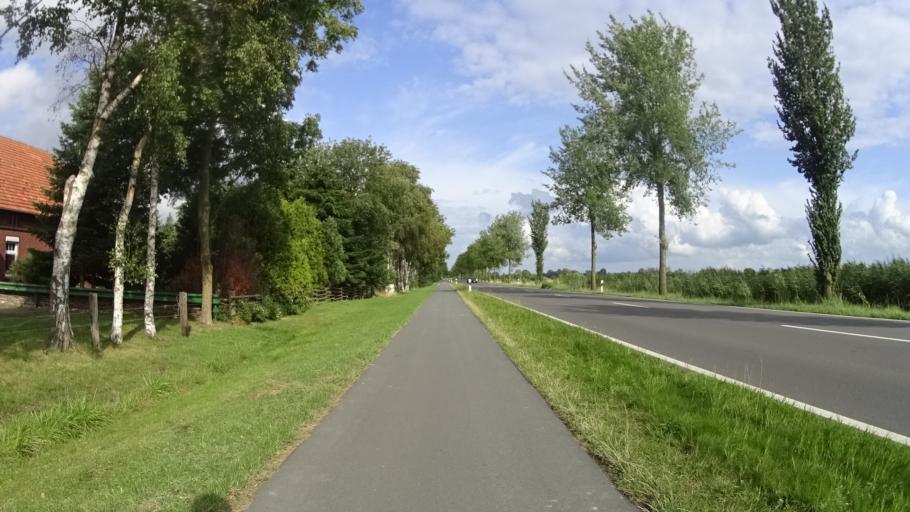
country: DE
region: Lower Saxony
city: Varel
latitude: 53.3867
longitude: 8.2129
